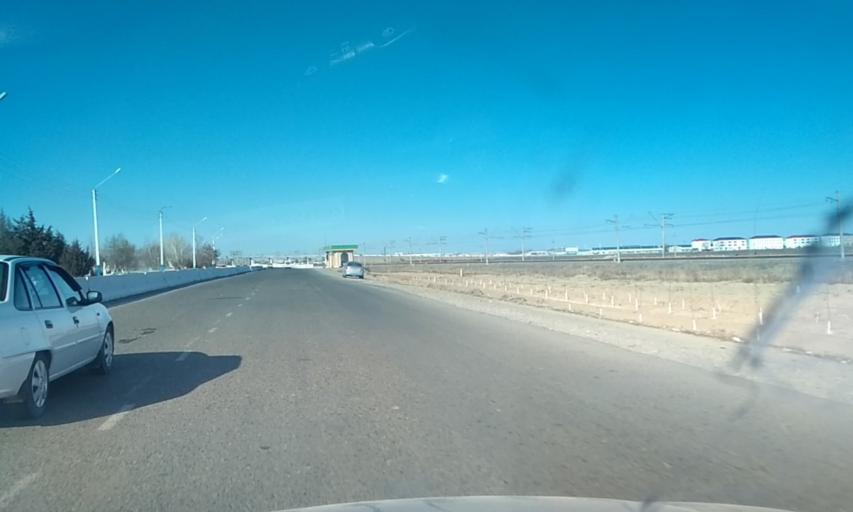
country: UZ
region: Sirdaryo
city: Guliston
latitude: 40.4673
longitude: 68.7720
